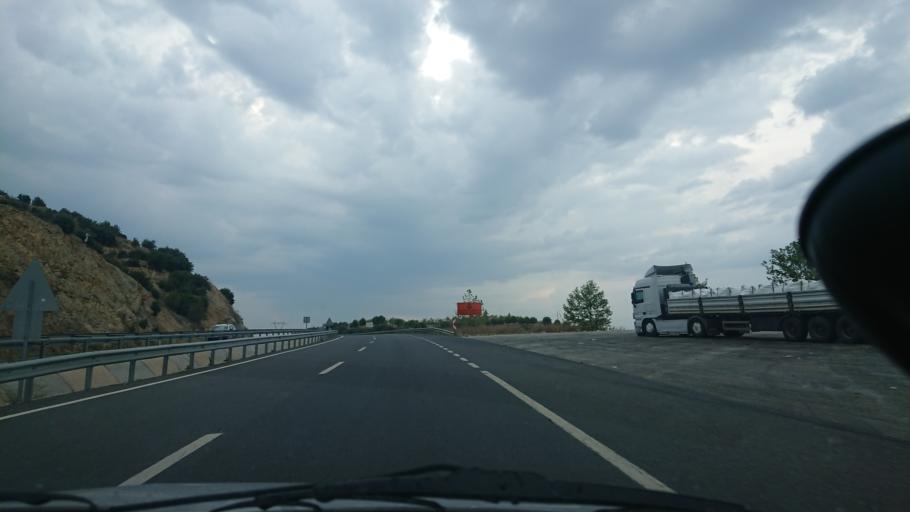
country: TR
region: Manisa
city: Selendi
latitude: 38.6288
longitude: 28.9389
